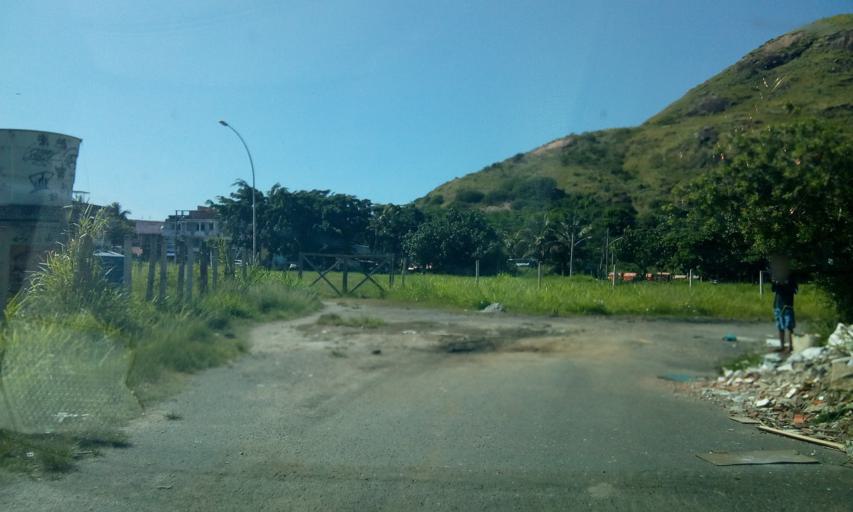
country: BR
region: Rio de Janeiro
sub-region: Nilopolis
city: Nilopolis
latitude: -23.0253
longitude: -43.4864
